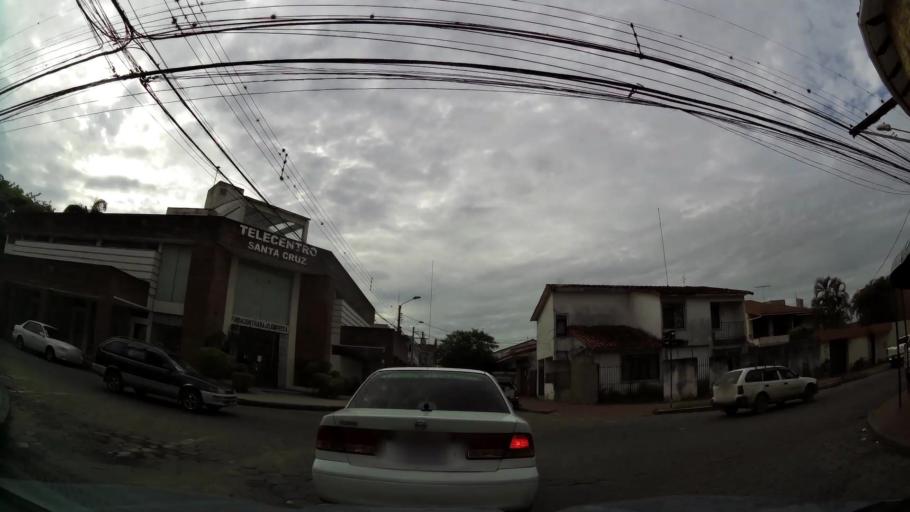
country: BO
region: Santa Cruz
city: Santa Cruz de la Sierra
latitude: -17.7884
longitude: -63.1742
